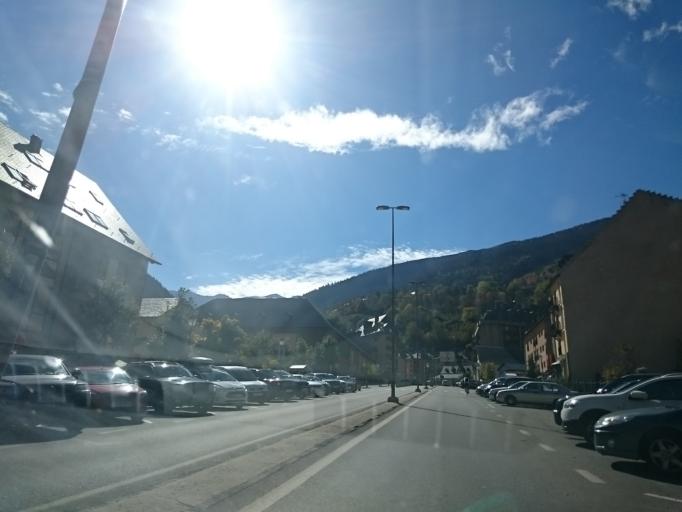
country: ES
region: Catalonia
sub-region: Provincia de Lleida
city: Vielha
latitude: 42.7045
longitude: 0.7948
